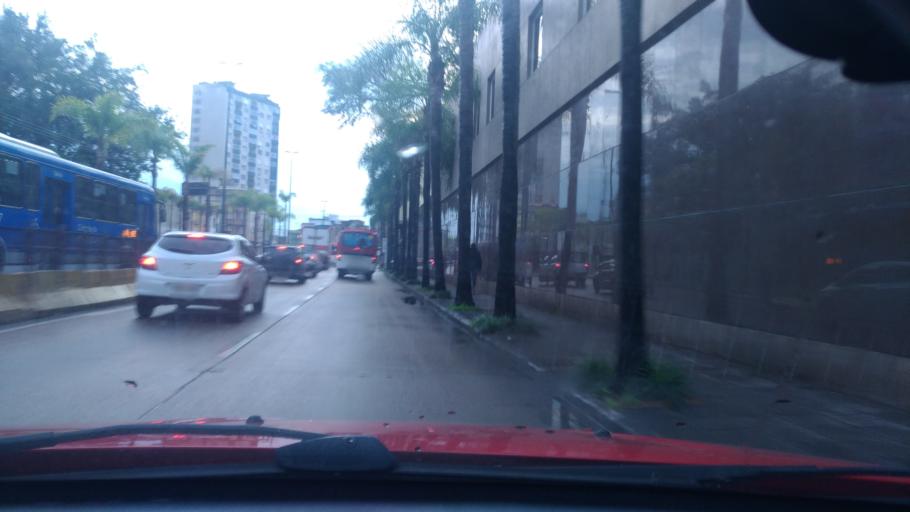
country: BR
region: Rio Grande do Sul
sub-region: Porto Alegre
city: Porto Alegre
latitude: -30.0156
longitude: -51.2062
